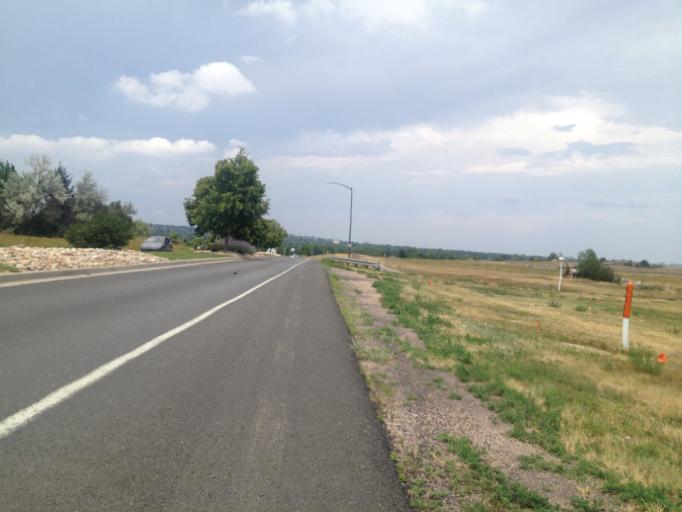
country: US
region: Colorado
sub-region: Boulder County
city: Superior
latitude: 39.9536
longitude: -105.1469
